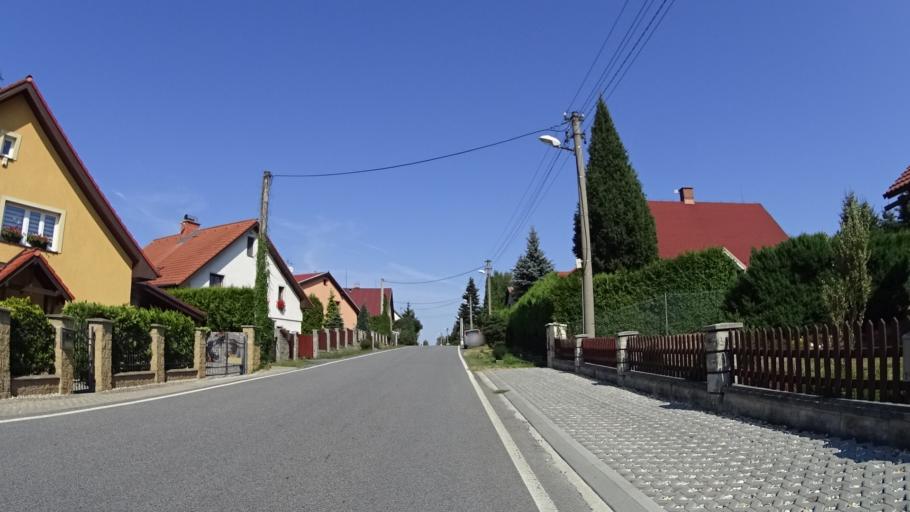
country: CZ
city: Chrastava
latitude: 50.7948
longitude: 14.9904
